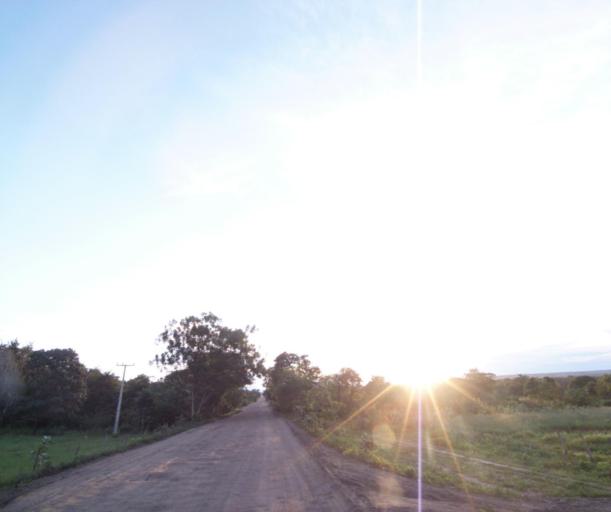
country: BR
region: Bahia
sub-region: Sao Felix Do Coribe
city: Santa Maria da Vitoria
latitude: -13.6275
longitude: -44.4229
